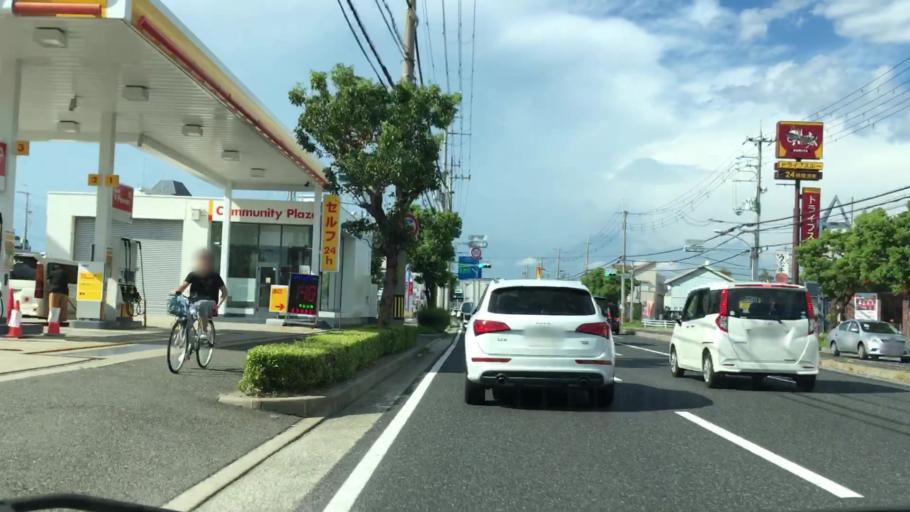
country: JP
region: Hyogo
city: Akashi
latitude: 34.6814
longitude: 134.9822
